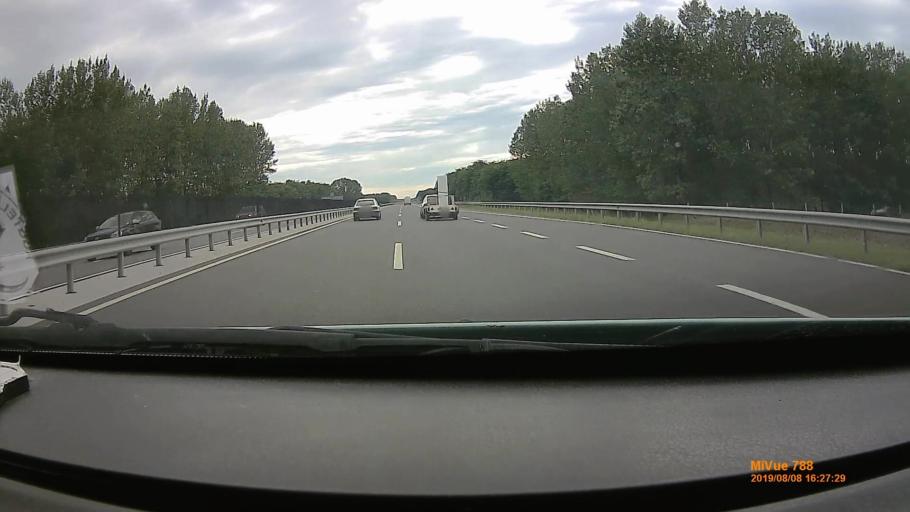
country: HU
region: Szabolcs-Szatmar-Bereg
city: Vaja
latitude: 47.9648
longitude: 22.1913
